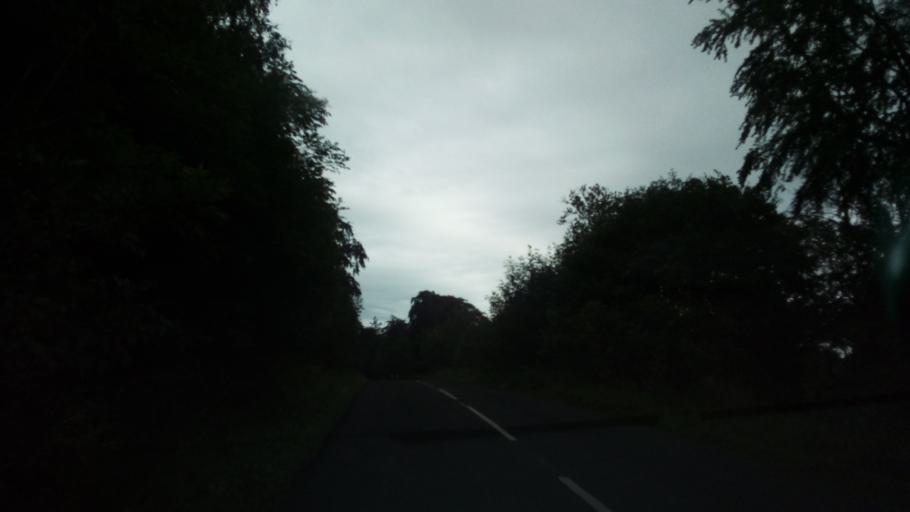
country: GB
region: England
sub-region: County Durham
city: Holwick
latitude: 54.5909
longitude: -2.1583
